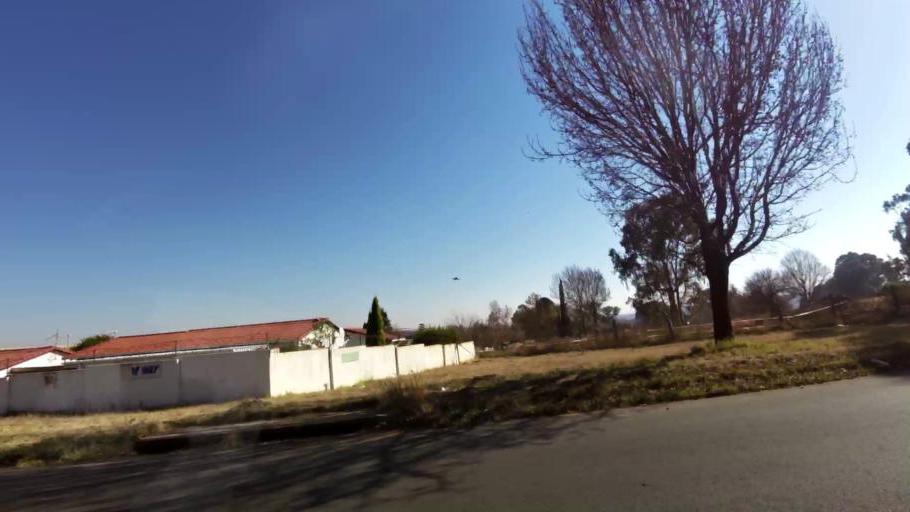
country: ZA
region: Gauteng
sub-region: City of Johannesburg Metropolitan Municipality
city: Johannesburg
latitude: -26.2463
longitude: 27.9953
